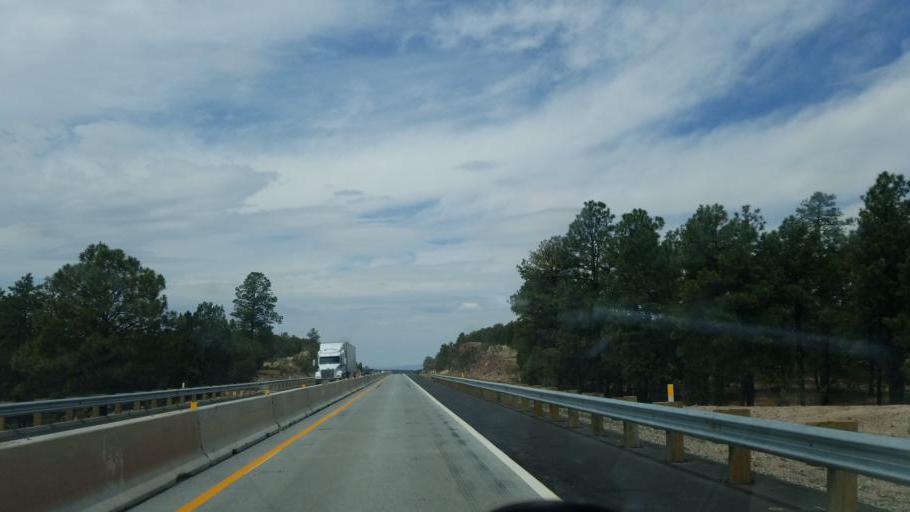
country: US
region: Arizona
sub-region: Coconino County
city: Williams
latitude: 35.2226
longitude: -112.2498
